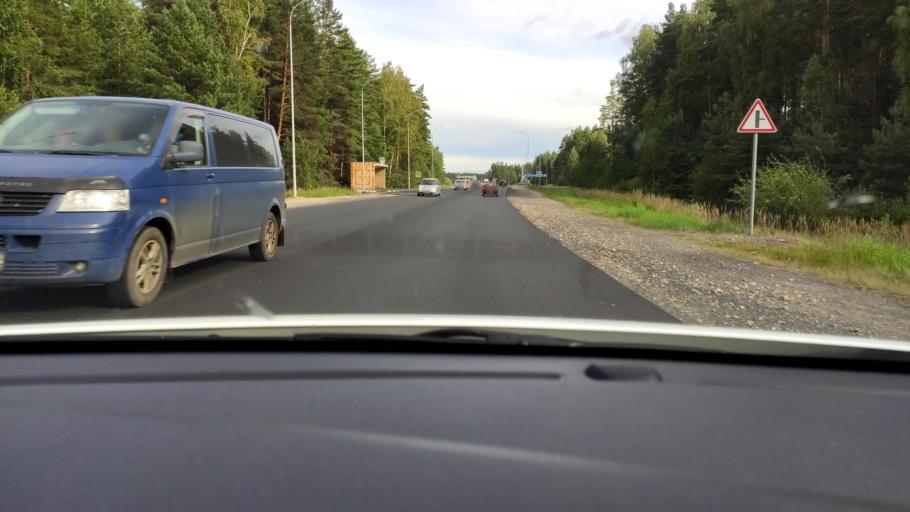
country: RU
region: Mariy-El
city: Yoshkar-Ola
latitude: 56.5390
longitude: 47.9873
